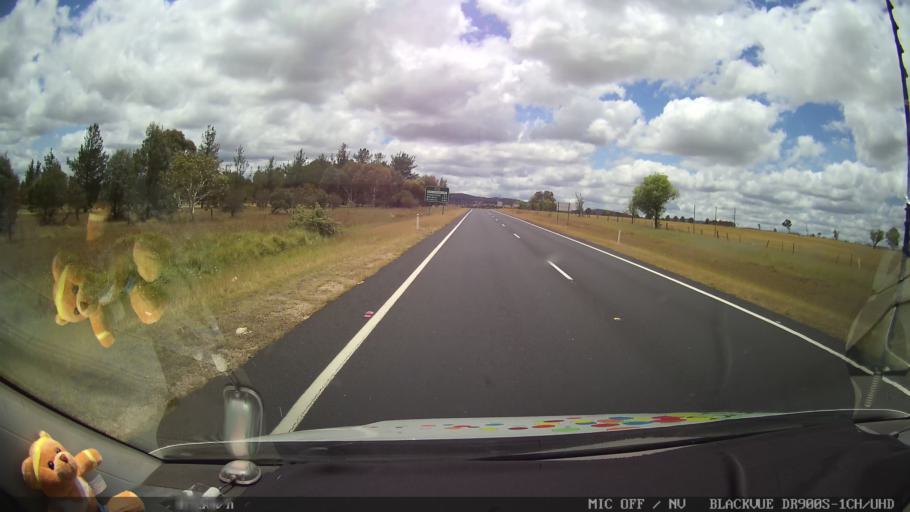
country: AU
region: New South Wales
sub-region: Glen Innes Severn
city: Glen Innes
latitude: -29.4347
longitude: 151.8498
